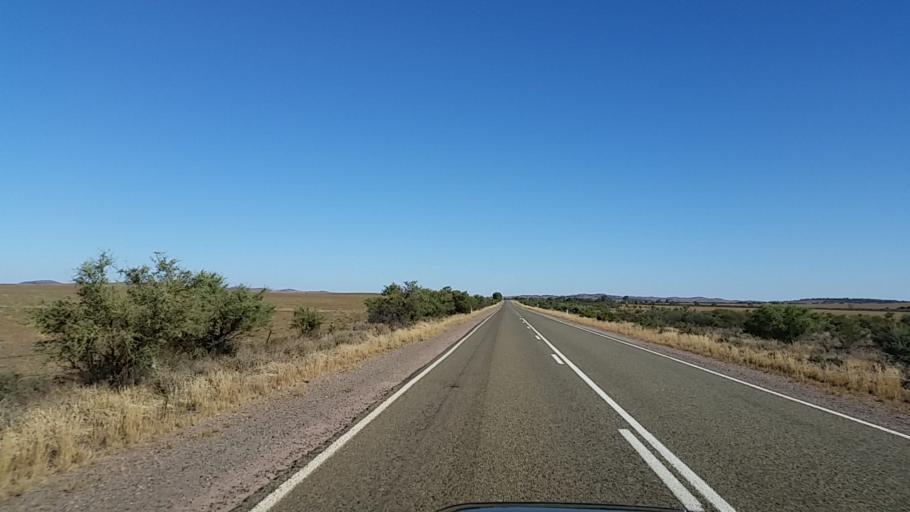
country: AU
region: South Australia
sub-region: Flinders Ranges
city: Quorn
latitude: -32.4399
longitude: 138.5355
